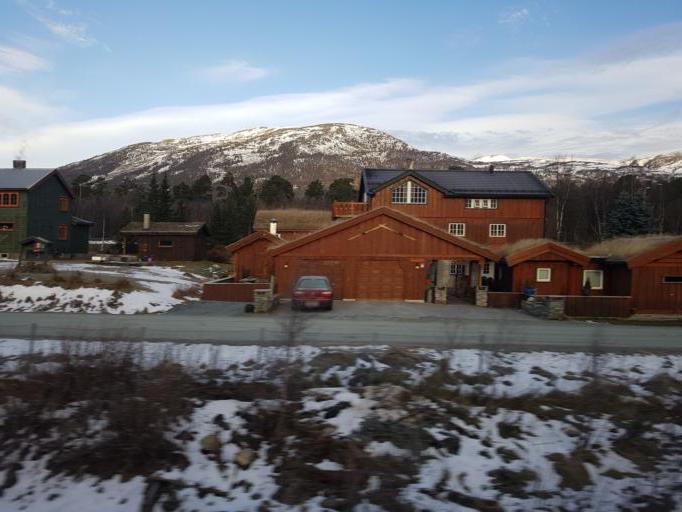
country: NO
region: Sor-Trondelag
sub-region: Oppdal
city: Oppdal
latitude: 62.5980
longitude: 9.7061
